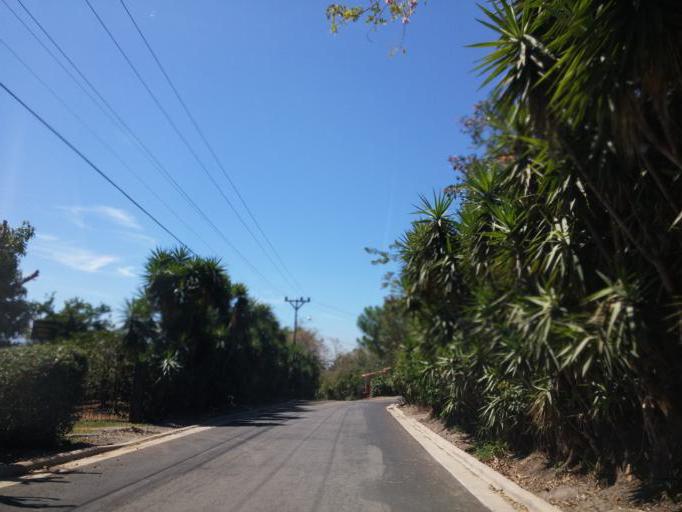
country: CR
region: Alajuela
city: Sabanilla
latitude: 10.0696
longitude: -84.2066
